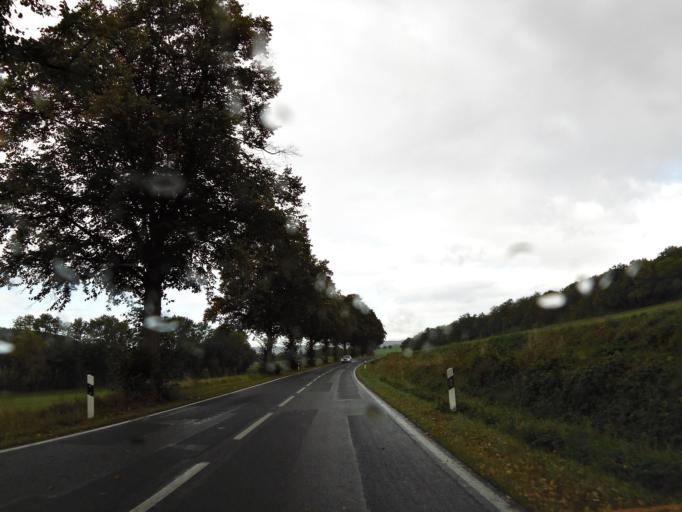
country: DE
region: Lower Saxony
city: Rosdorf
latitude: 51.4571
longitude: 9.9080
